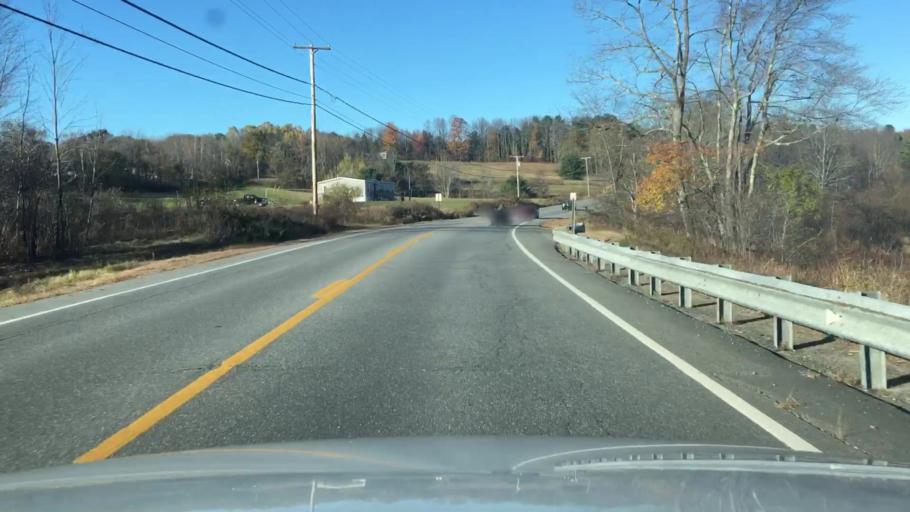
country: US
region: Maine
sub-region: Sagadahoc County
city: Topsham
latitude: 44.0353
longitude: -69.9435
